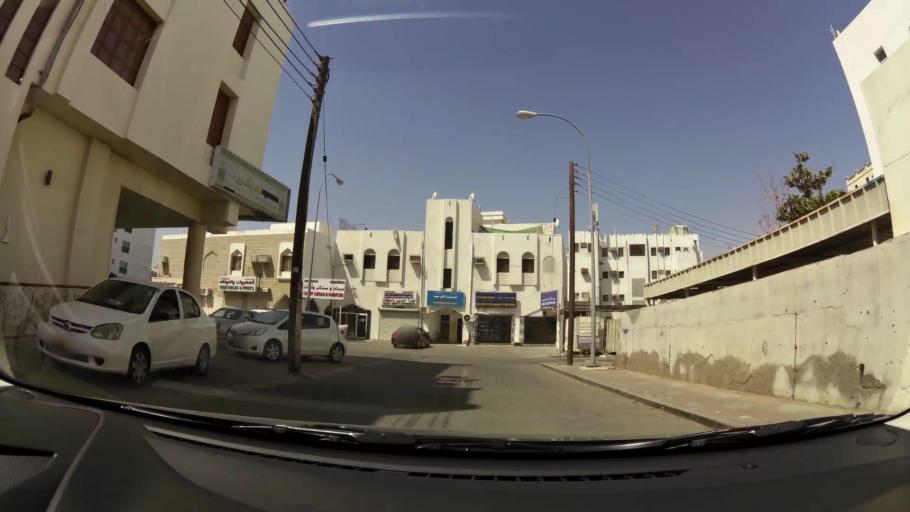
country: OM
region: Muhafazat Masqat
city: Bawshar
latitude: 23.5908
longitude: 58.4058
